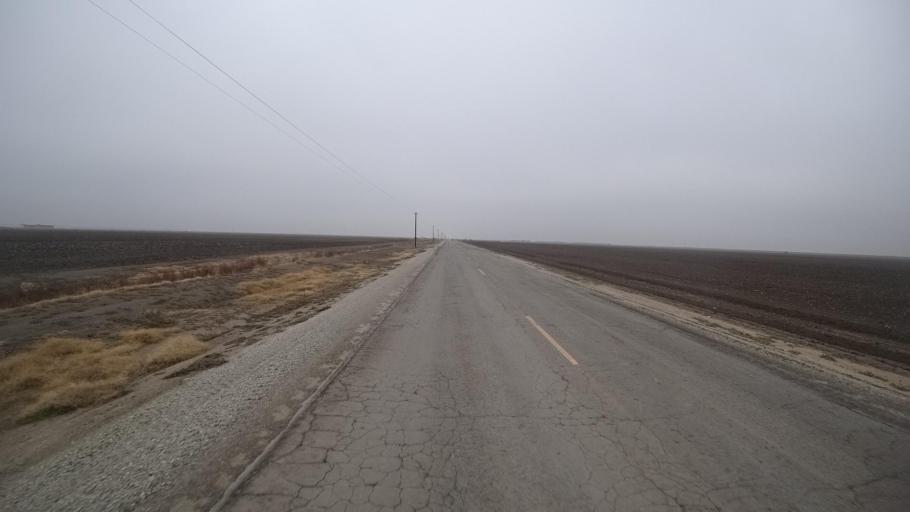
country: US
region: California
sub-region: Kern County
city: Greenfield
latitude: 35.1679
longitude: -119.1990
